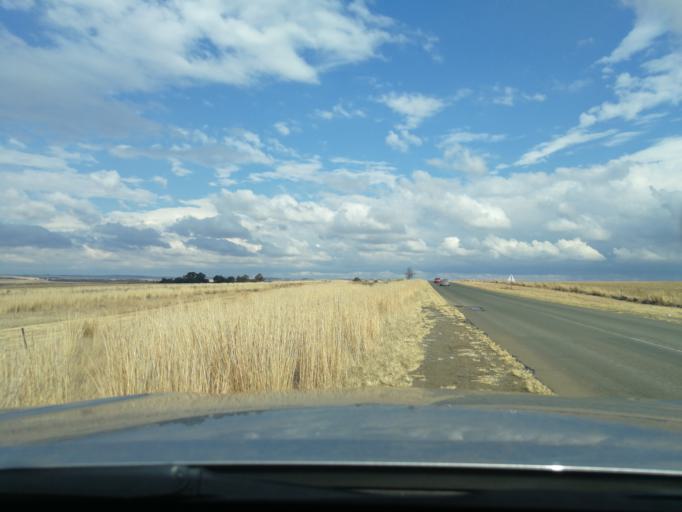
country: ZA
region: Orange Free State
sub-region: Fezile Dabi District Municipality
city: Frankfort
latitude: -27.4391
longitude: 28.5131
